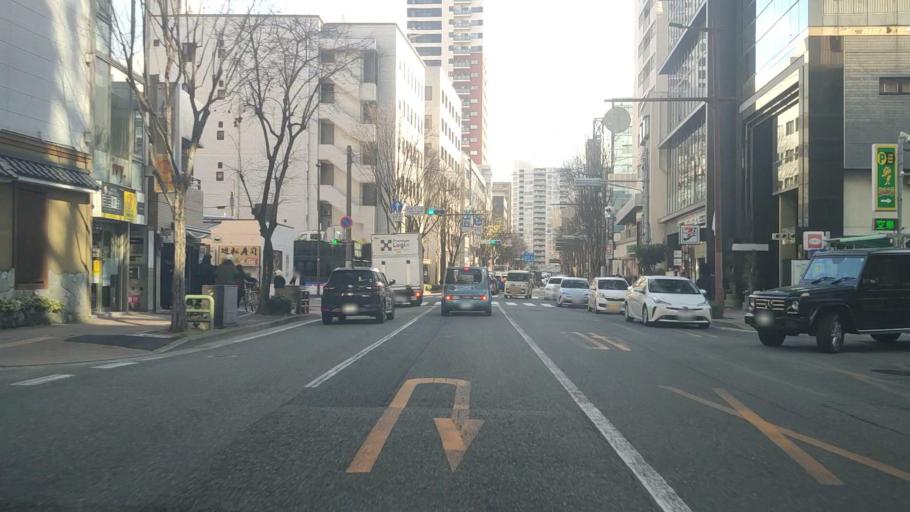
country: JP
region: Fukuoka
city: Fukuoka-shi
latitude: 33.5884
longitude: 130.3908
